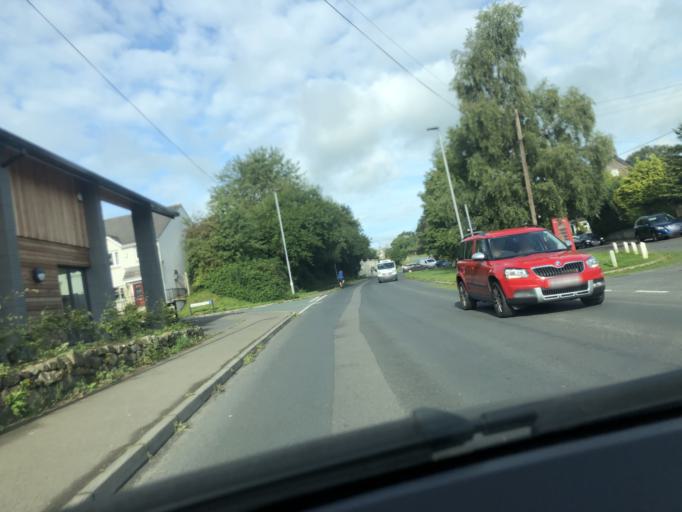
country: GB
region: England
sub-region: Cornwall
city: Launceston
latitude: 50.6433
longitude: -4.2856
